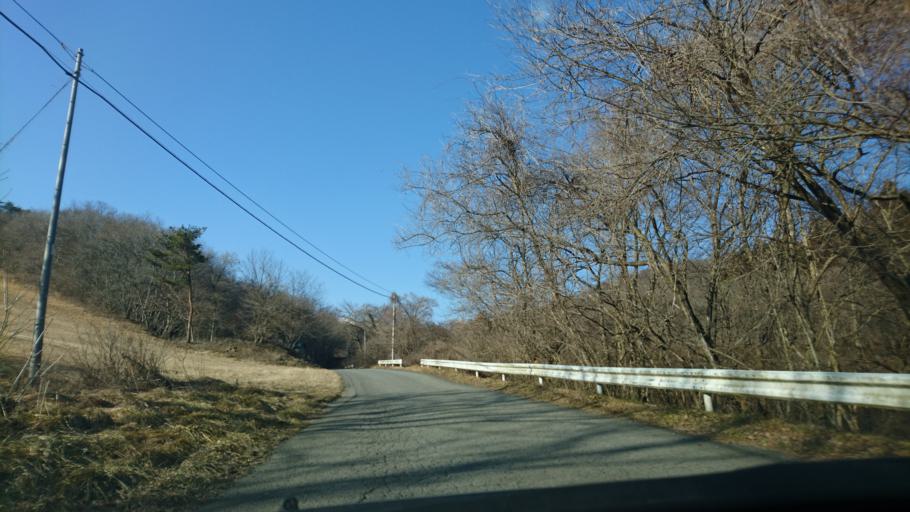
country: JP
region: Iwate
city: Ichinoseki
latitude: 38.8075
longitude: 141.2906
